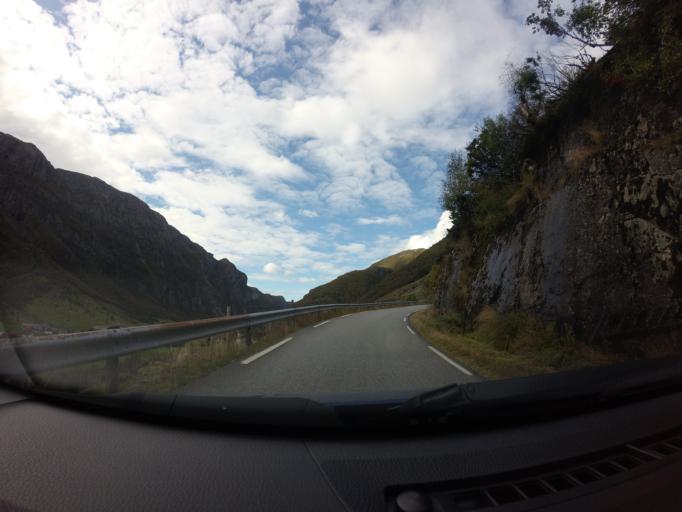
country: NO
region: Rogaland
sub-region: Forsand
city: Forsand
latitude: 58.8485
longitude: 6.3656
